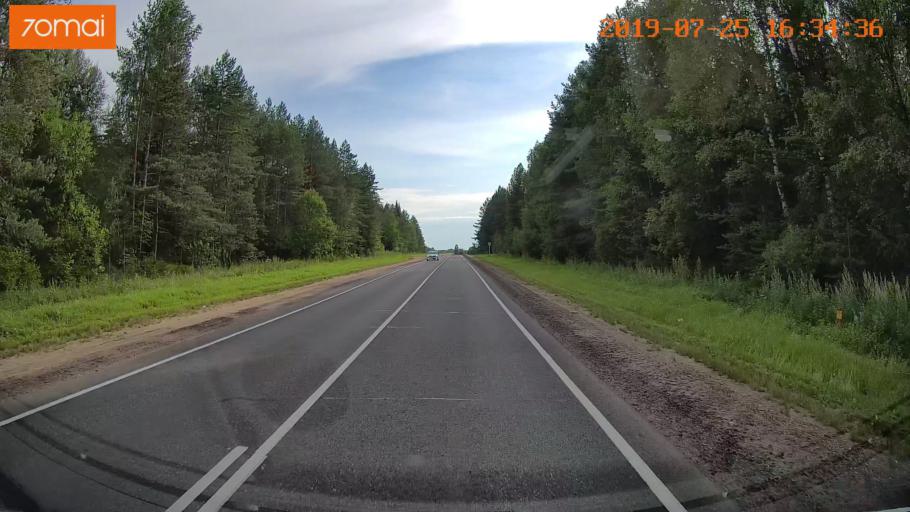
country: RU
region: Ivanovo
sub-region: Privolzhskiy Rayon
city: Ples
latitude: 57.4150
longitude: 41.4339
